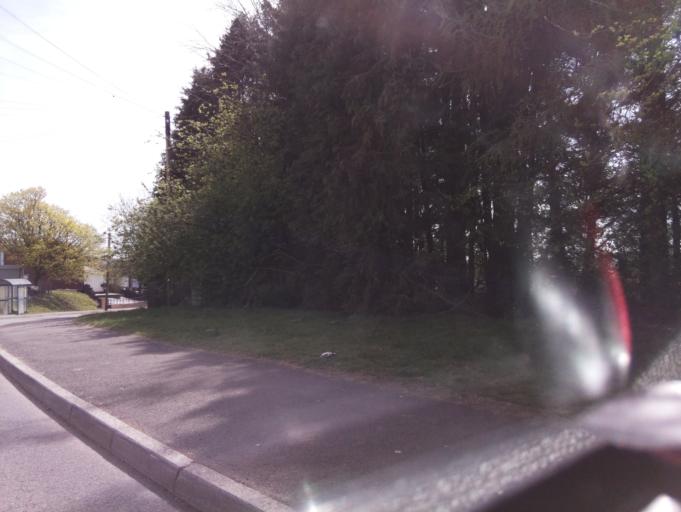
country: GB
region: Wales
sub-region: Merthyr Tydfil County Borough
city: Merthyr Tydfil
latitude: 51.7655
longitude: -3.3504
